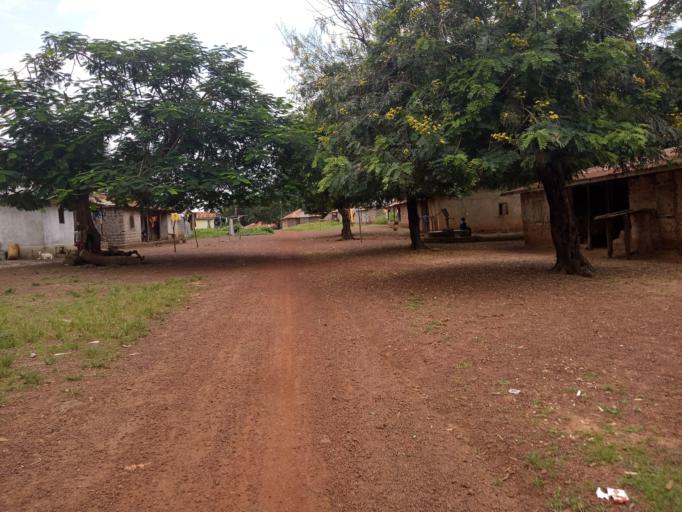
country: SL
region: Northern Province
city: Kamakwie
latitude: 9.4809
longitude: -12.2520
